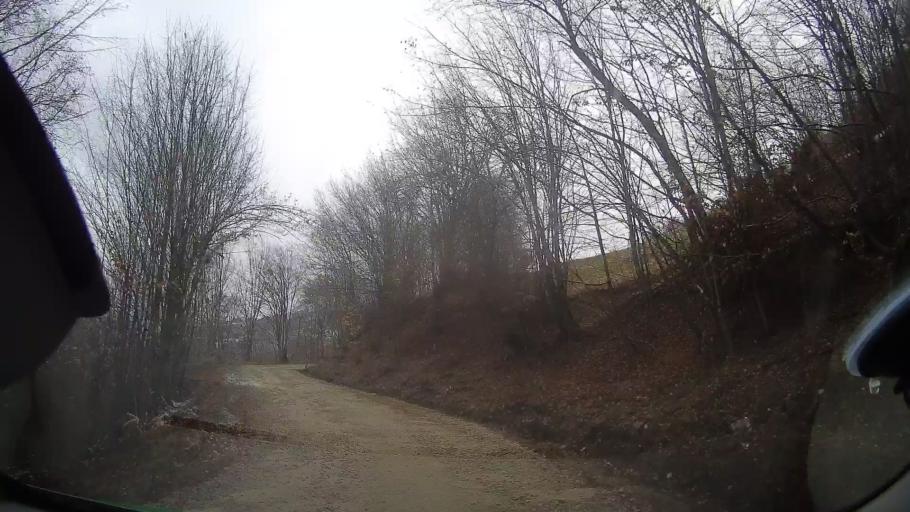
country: RO
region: Cluj
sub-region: Comuna Maguri-Racatau
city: Maguri-Racatau
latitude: 46.6541
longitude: 23.1890
